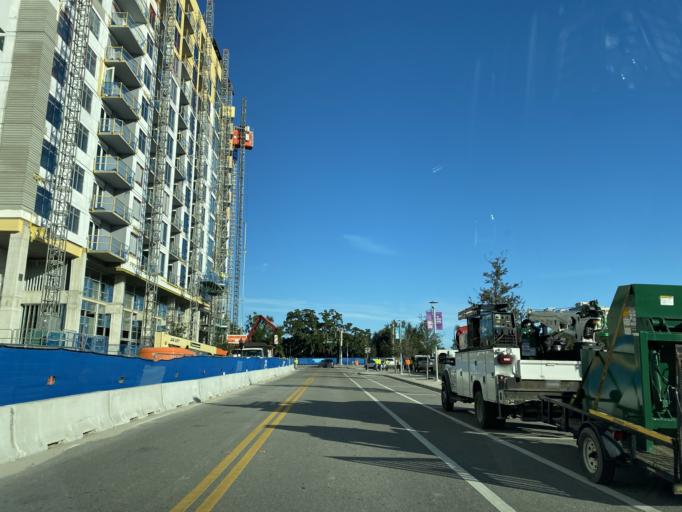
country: US
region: Florida
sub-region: Orange County
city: Orlando
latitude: 28.5487
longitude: -81.3871
